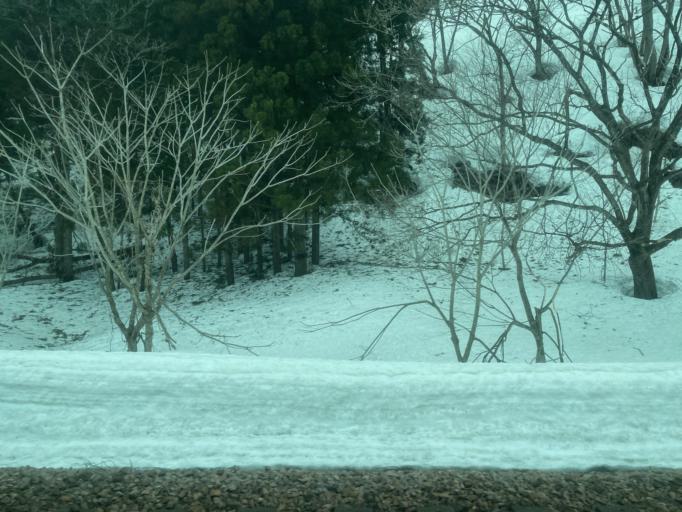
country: JP
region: Niigata
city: Shiozawa
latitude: 36.9318
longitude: 138.8177
